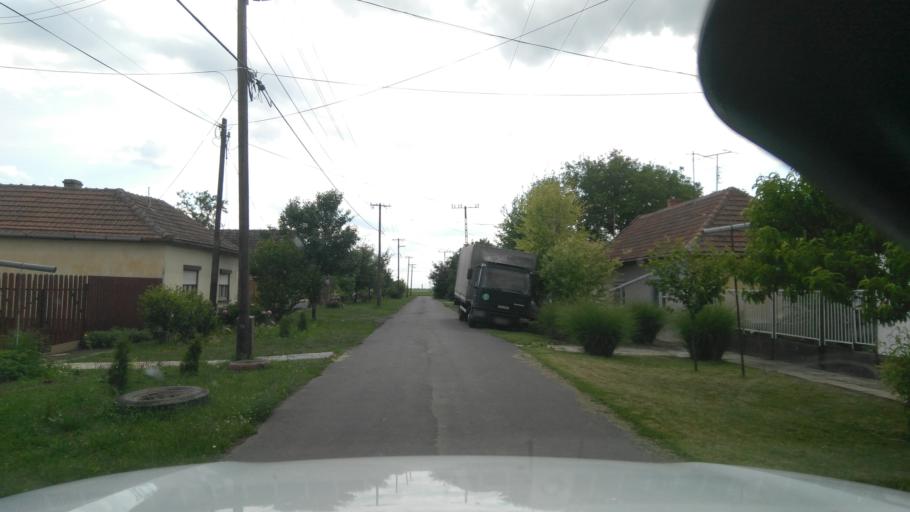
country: HU
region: Bekes
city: Magyarbanhegyes
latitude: 46.4490
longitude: 20.9728
